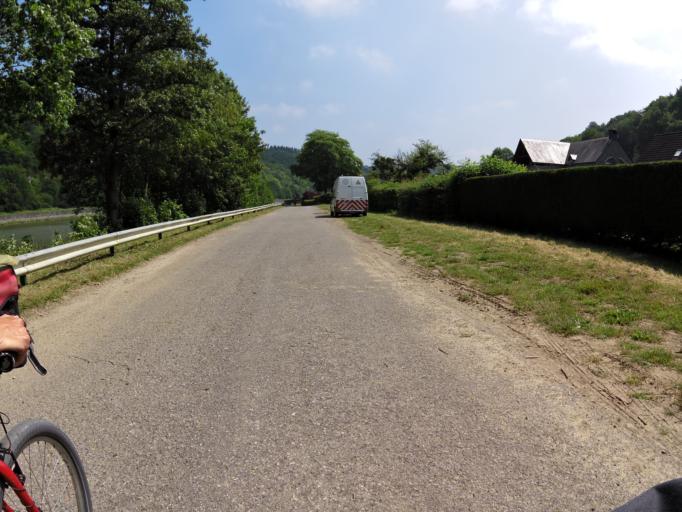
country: BE
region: Wallonia
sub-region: Province de Namur
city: Hastiere-Lavaux
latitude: 50.2129
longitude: 4.8435
